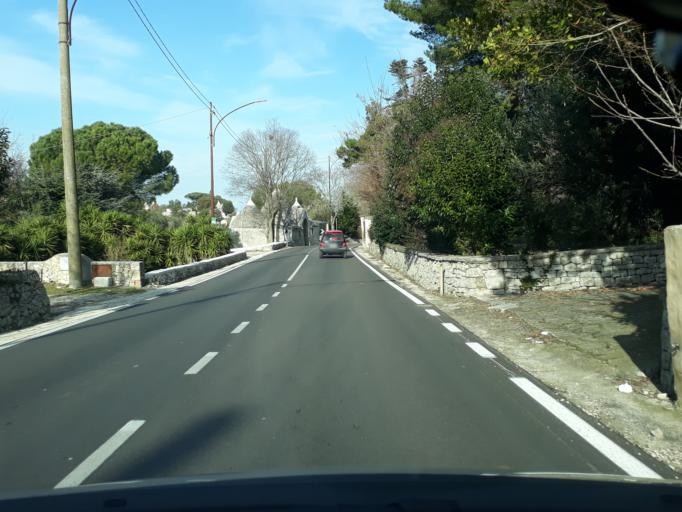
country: IT
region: Apulia
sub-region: Provincia di Brindisi
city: Lamie di Olimpie-Selva
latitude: 40.7982
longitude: 17.3519
